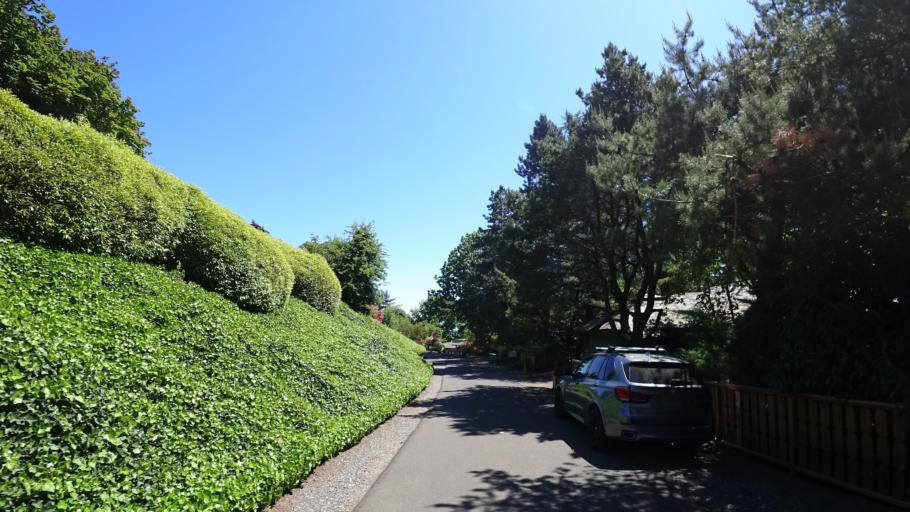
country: US
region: Oregon
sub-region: Washington County
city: West Slope
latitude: 45.5017
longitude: -122.7243
